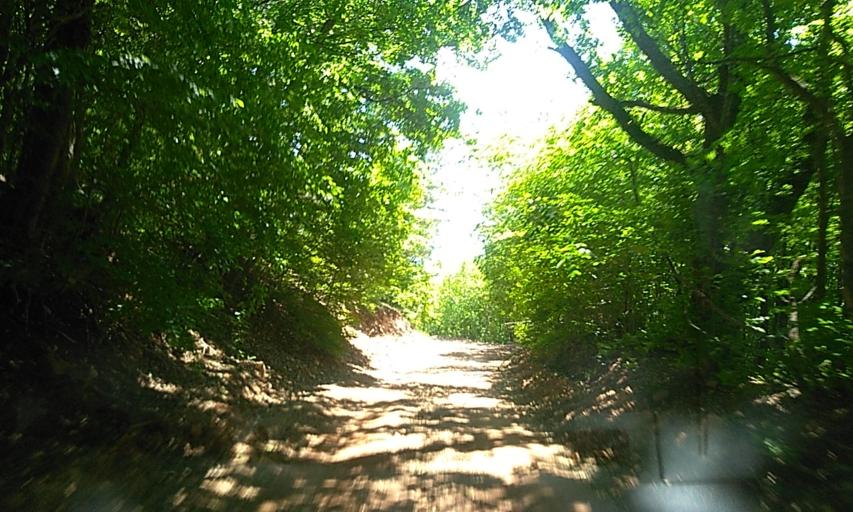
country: RS
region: Central Serbia
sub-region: Nisavski Okrug
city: Niska Banja
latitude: 43.3725
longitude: 21.9916
